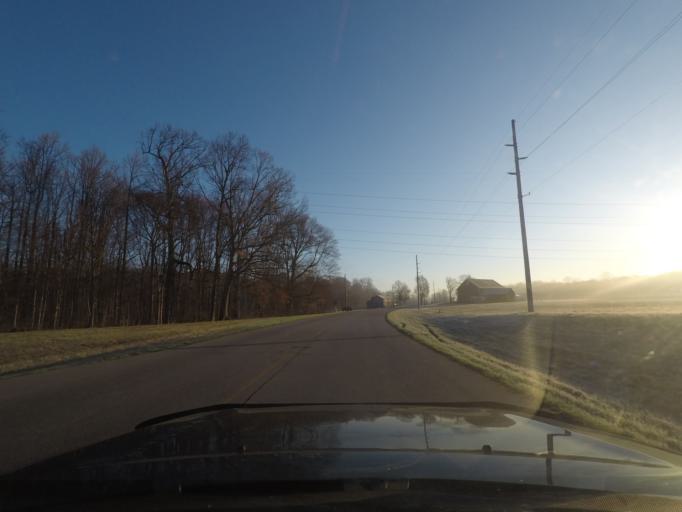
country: US
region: Indiana
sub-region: Marshall County
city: Bremen
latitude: 41.4535
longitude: -86.0941
